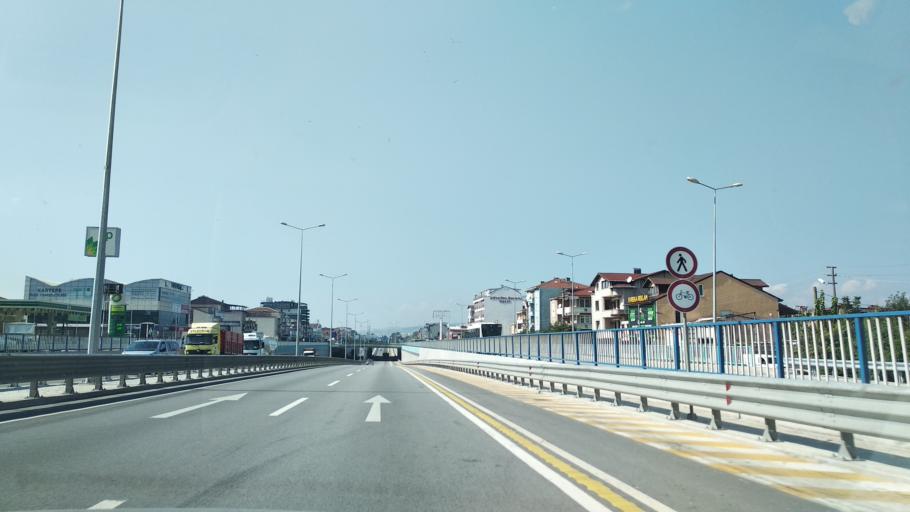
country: TR
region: Kocaeli
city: Kosekoy
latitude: 40.7529
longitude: 30.0272
